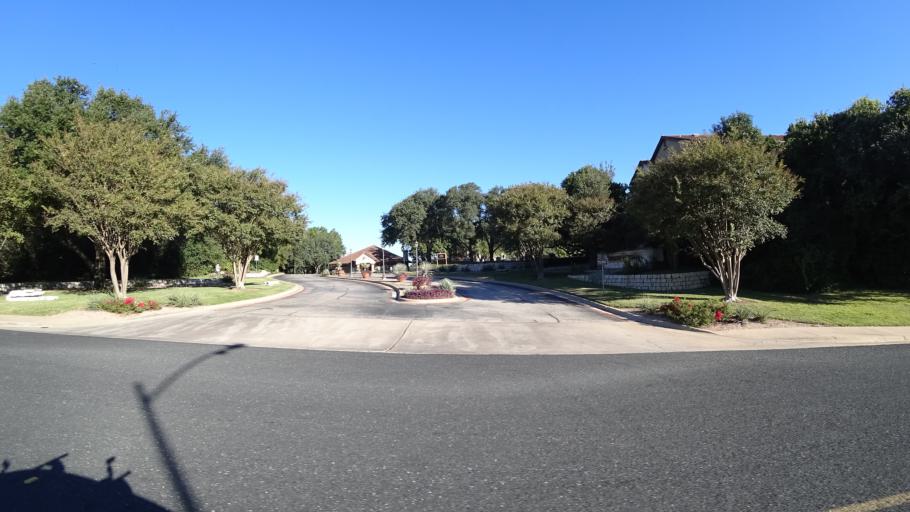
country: US
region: Texas
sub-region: Travis County
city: West Lake Hills
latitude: 30.3578
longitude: -97.7956
